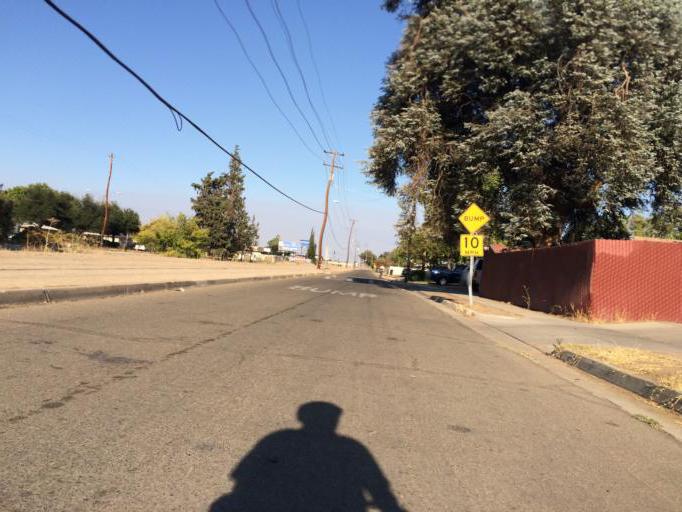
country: US
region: California
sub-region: Fresno County
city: Fresno
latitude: 36.7646
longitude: -119.7678
